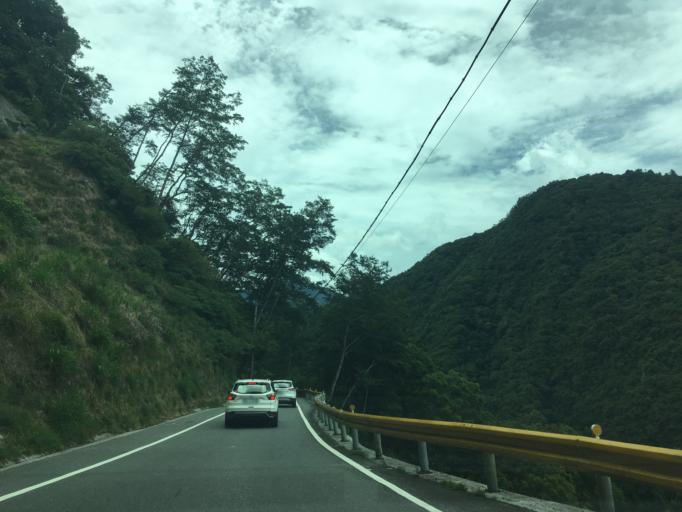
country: TW
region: Taiwan
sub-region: Hualien
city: Hualian
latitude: 24.1891
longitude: 121.4087
